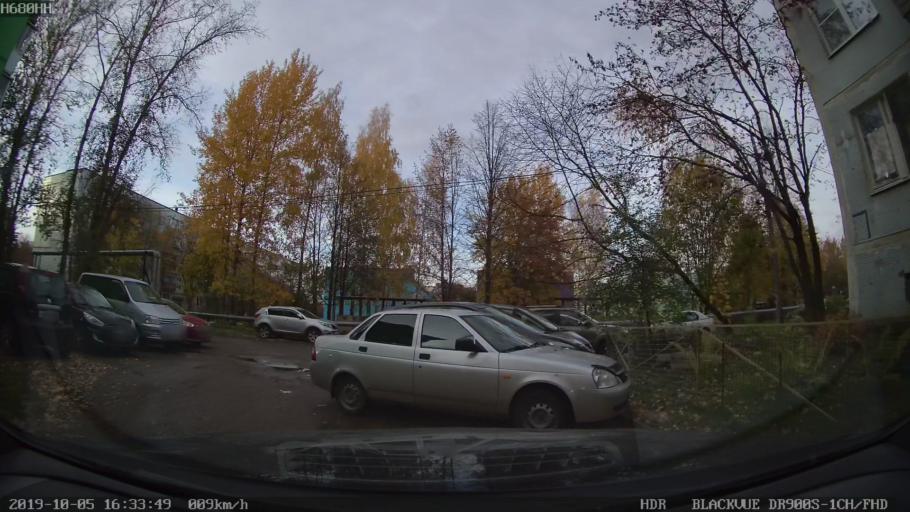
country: RU
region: Moskovskaya
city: Solnechnogorsk
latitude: 56.2177
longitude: 37.0320
